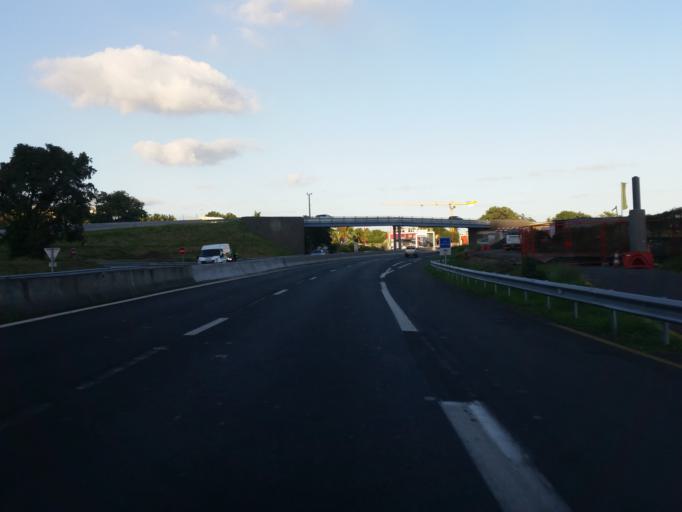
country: RE
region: Reunion
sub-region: Reunion
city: La Possession
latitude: -20.9220
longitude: 55.3451
